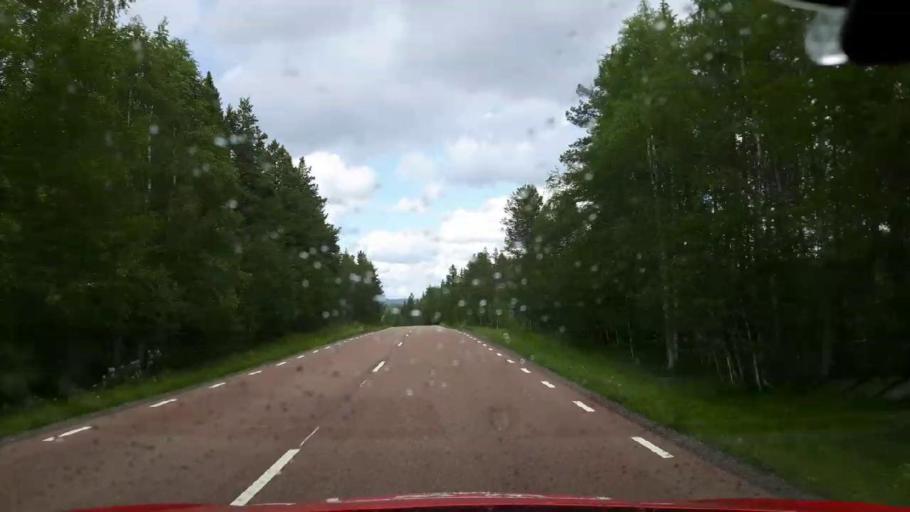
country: SE
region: Jaemtland
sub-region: Krokoms Kommun
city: Valla
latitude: 63.9405
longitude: 14.2230
